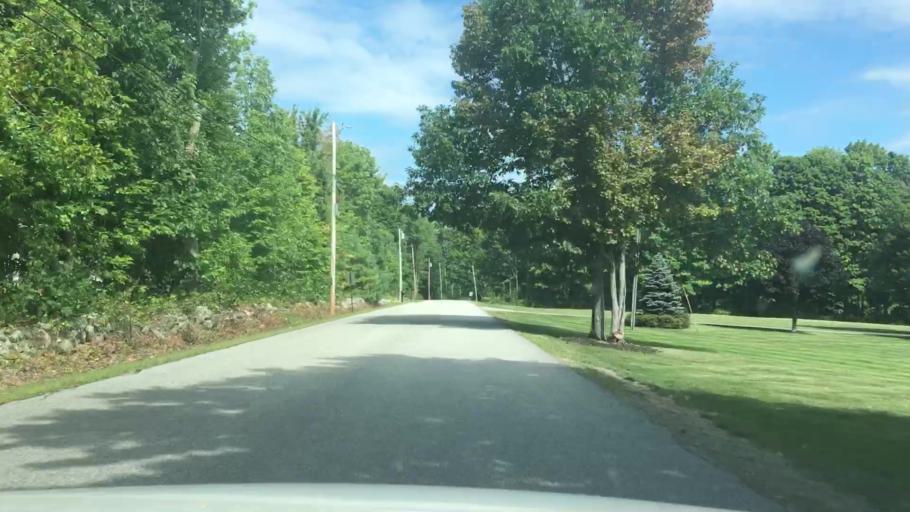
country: US
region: Maine
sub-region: Androscoggin County
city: Turner
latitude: 44.1773
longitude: -70.2530
